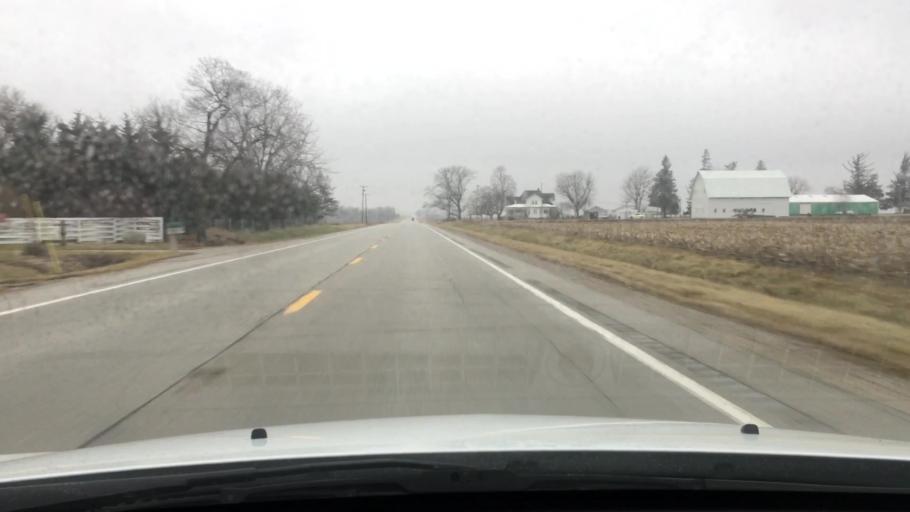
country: US
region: Illinois
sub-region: Livingston County
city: Flanagan
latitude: 40.8704
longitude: -88.8810
